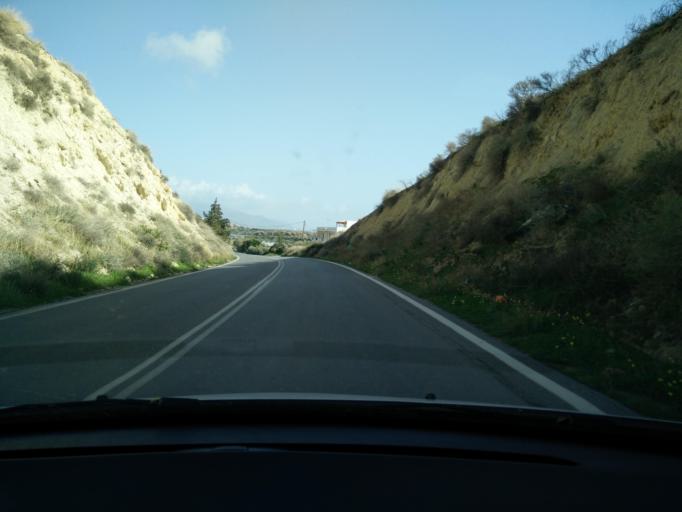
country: GR
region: Crete
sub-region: Nomos Lasithiou
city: Gra Liyia
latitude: 35.0078
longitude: 25.6361
